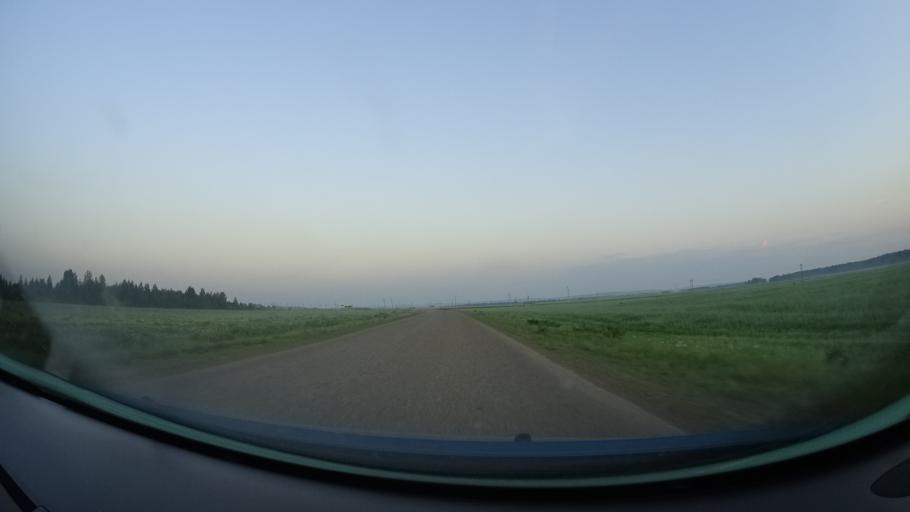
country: RU
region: Bashkortostan
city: Starobaltachevo
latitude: 56.0375
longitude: 55.9324
